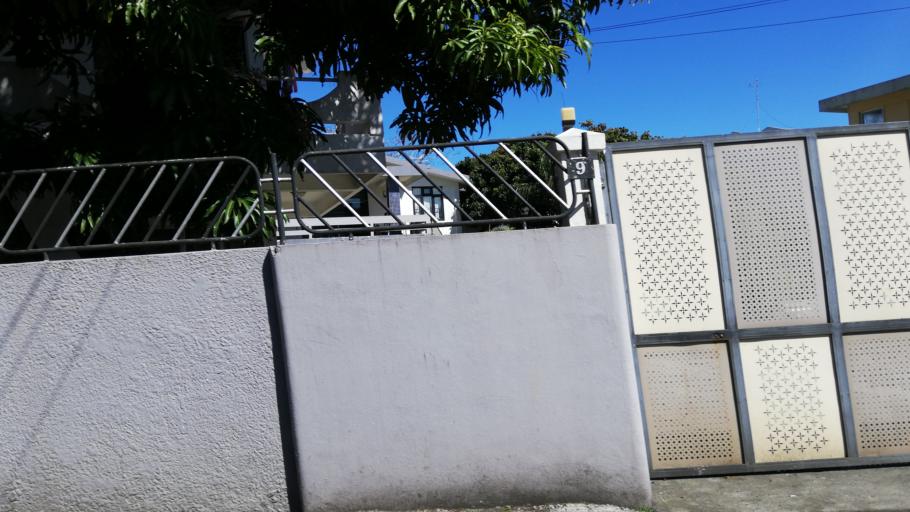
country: MU
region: Plaines Wilhems
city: Ebene
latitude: -20.2335
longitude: 57.4736
